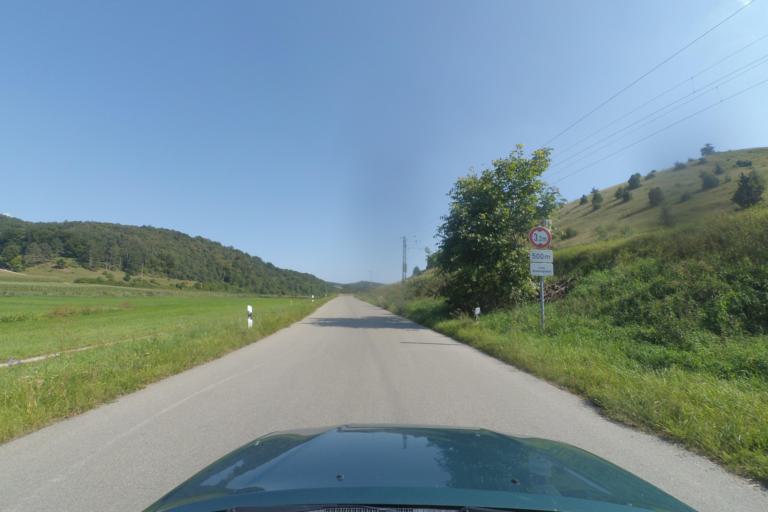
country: DE
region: Bavaria
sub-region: Swabia
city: Harburg
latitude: 48.8065
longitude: 10.6453
